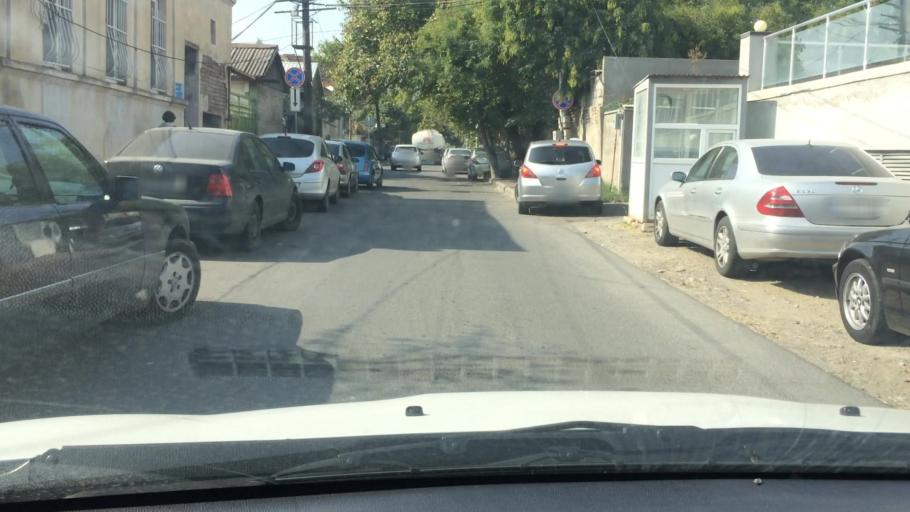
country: GE
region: T'bilisi
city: Tbilisi
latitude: 41.6907
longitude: 44.8274
